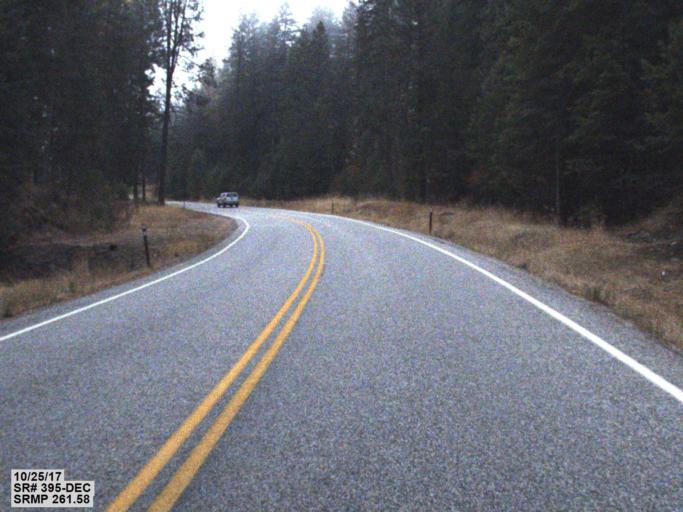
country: CA
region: British Columbia
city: Grand Forks
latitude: 48.8838
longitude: -118.2173
